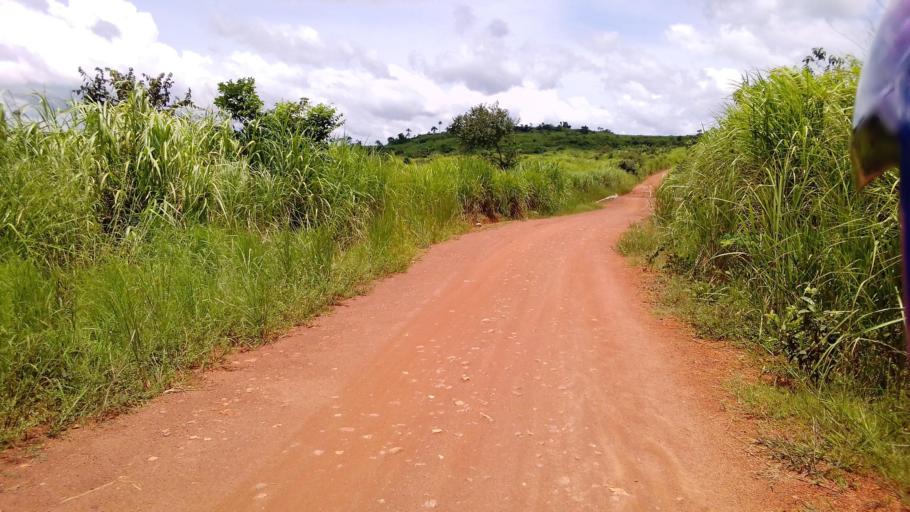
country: SL
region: Eastern Province
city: Koidu
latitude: 8.6783
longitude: -10.9360
